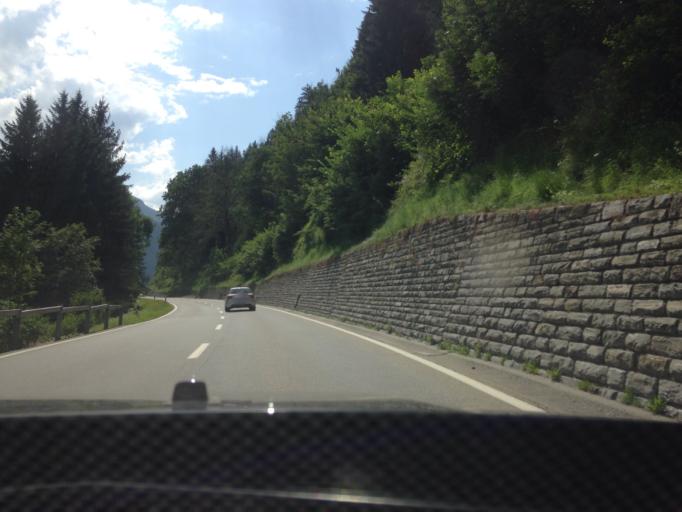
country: CH
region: Grisons
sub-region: Surselva District
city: Breil
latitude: 46.7711
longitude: 9.1168
